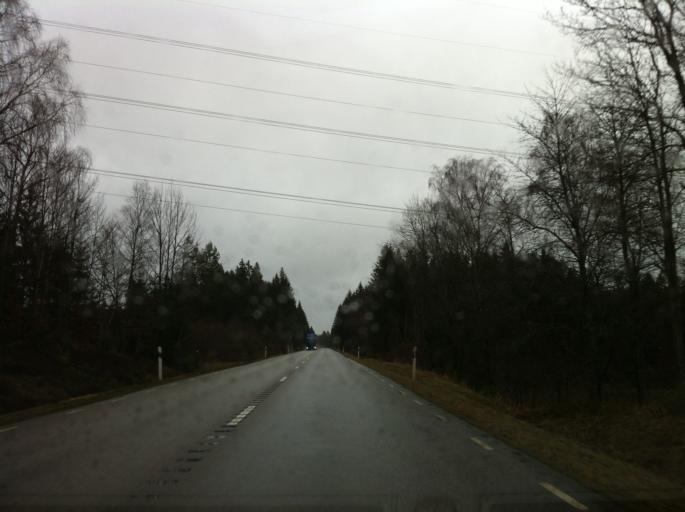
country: SE
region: Blekinge
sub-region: Olofstroms Kommun
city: Olofstroem
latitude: 56.3989
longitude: 14.6286
